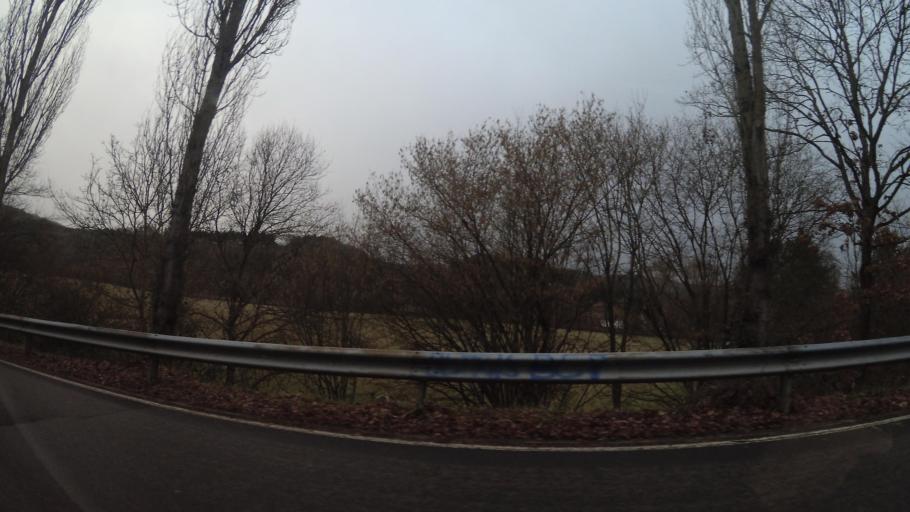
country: DE
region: Rheinland-Pfalz
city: Sankt Julian
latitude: 49.6091
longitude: 7.5282
